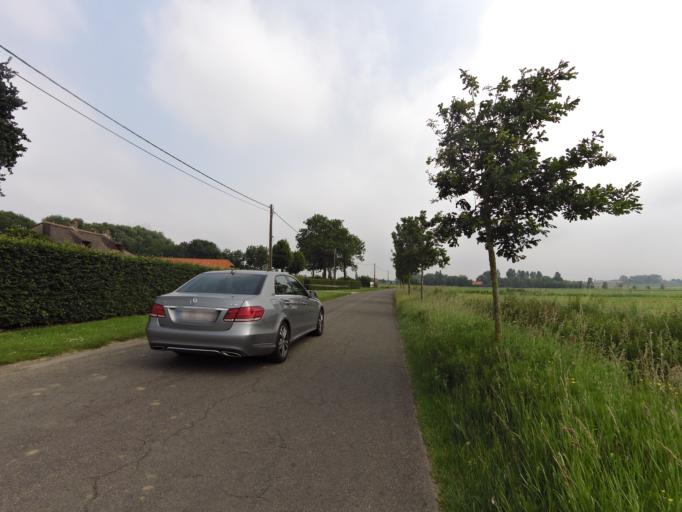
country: BE
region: Flanders
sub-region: Provincie West-Vlaanderen
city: Torhout
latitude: 51.1154
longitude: 3.0748
